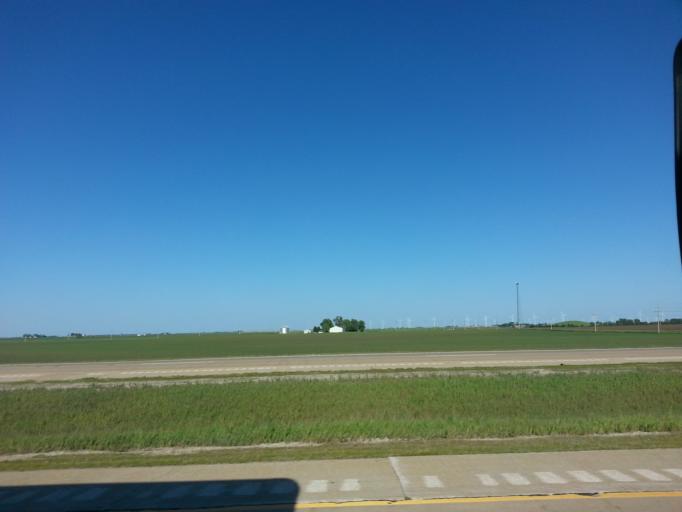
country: US
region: Illinois
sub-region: Woodford County
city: Minonk
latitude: 40.9274
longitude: -89.0568
